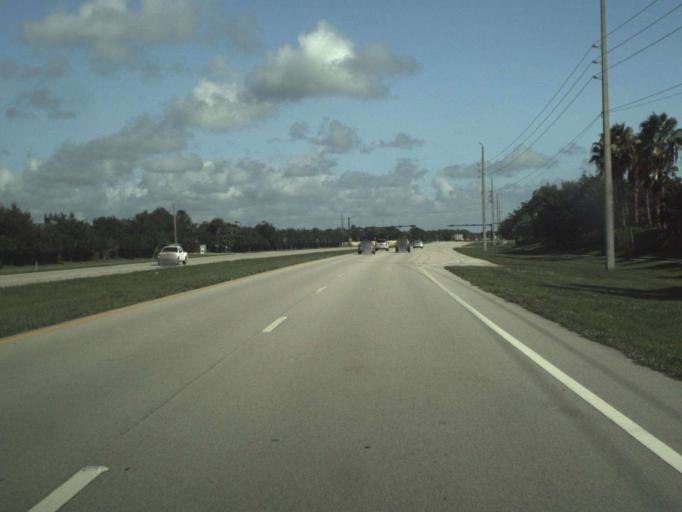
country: US
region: Florida
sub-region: Indian River County
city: Gifford
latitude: 27.6719
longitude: -80.3981
